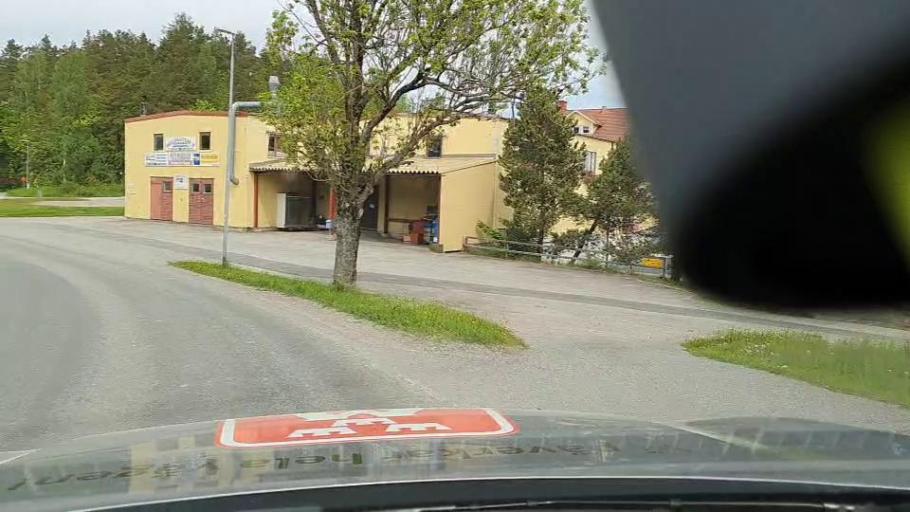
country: SE
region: Soedermanland
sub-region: Flens Kommun
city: Flen
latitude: 59.1002
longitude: 16.5551
